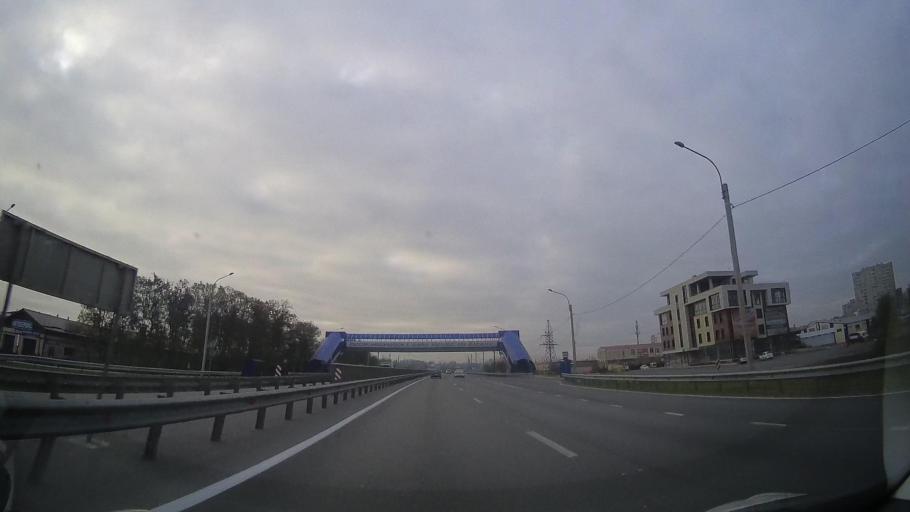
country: RU
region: Rostov
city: Bataysk
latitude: 47.1399
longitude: 39.7762
